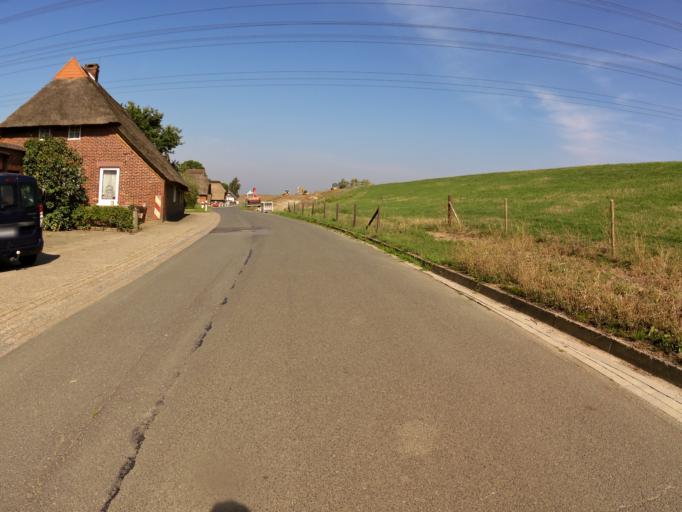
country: DE
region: Lower Saxony
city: Neuenkirchen
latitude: 53.1992
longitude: 8.4982
